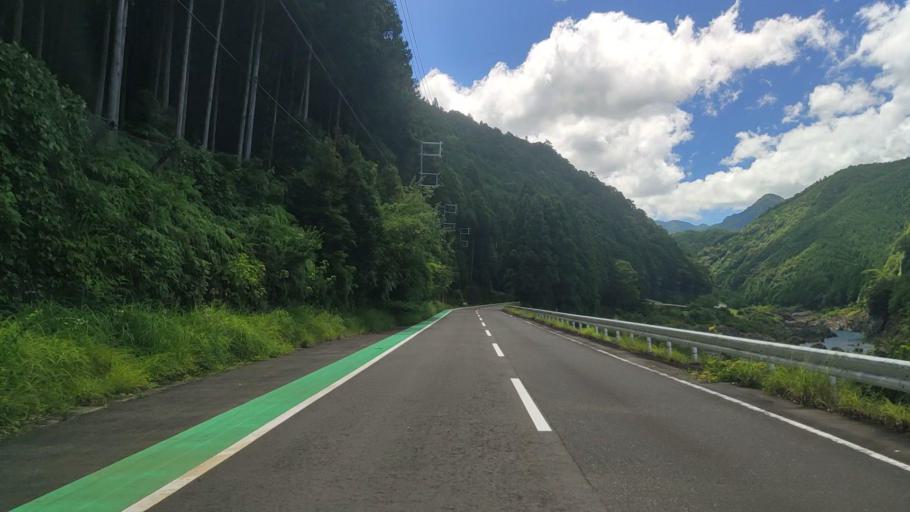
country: JP
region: Mie
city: Owase
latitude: 33.9655
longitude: 135.9921
